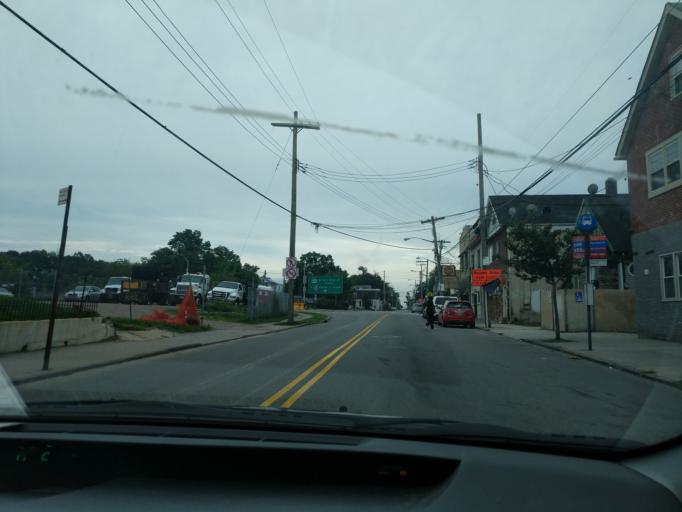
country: US
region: New York
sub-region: Richmond County
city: Bloomfield
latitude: 40.6325
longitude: -74.1465
